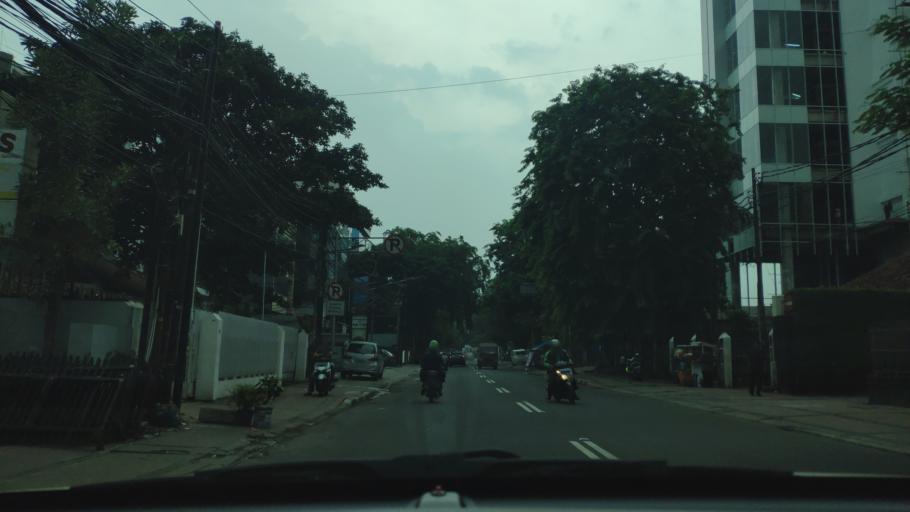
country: ID
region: Jakarta Raya
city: Jakarta
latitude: -6.1755
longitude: 106.8149
